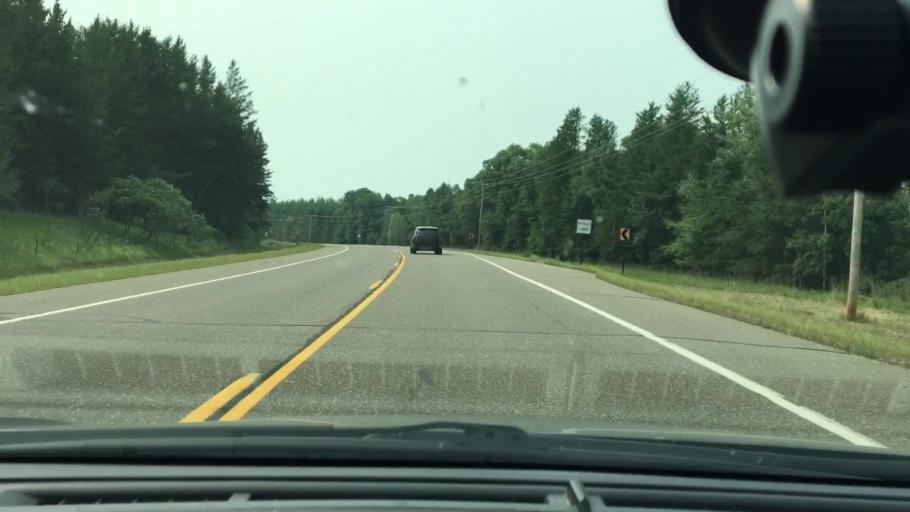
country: US
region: Minnesota
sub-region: Crow Wing County
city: Breezy Point
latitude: 46.5605
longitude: -94.1348
